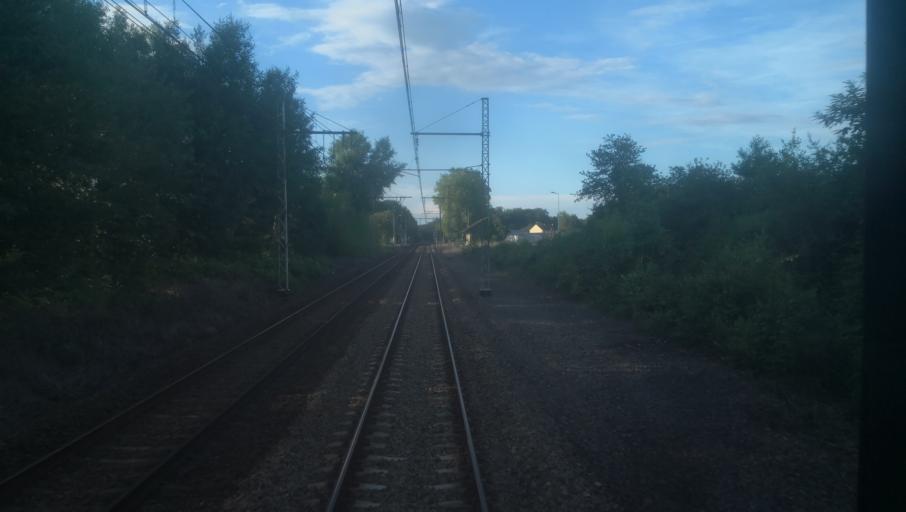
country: FR
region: Centre
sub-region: Departement de l'Indre
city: Luant
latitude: 46.7329
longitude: 1.5887
